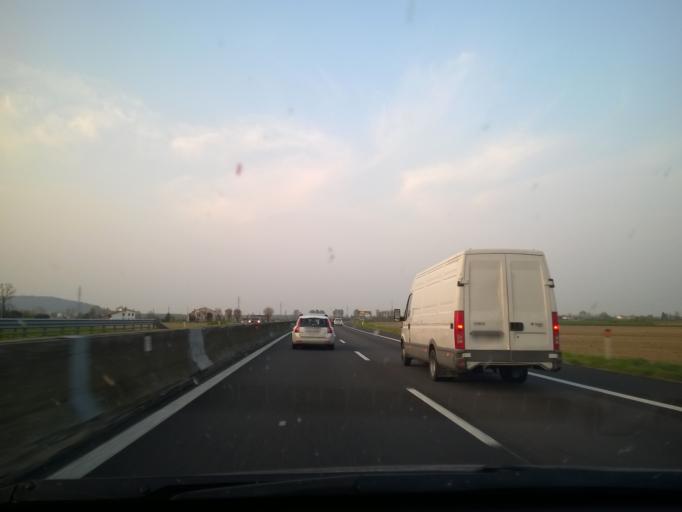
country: IT
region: Veneto
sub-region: Provincia di Padova
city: Battaglia Terme
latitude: 45.2728
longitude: 11.7852
